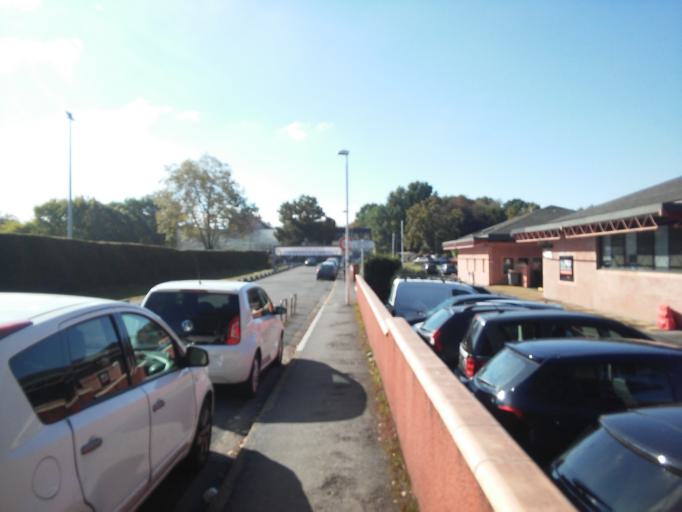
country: FR
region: Aquitaine
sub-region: Departement des Pyrenees-Atlantiques
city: Pau
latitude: 43.3180
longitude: -0.3643
